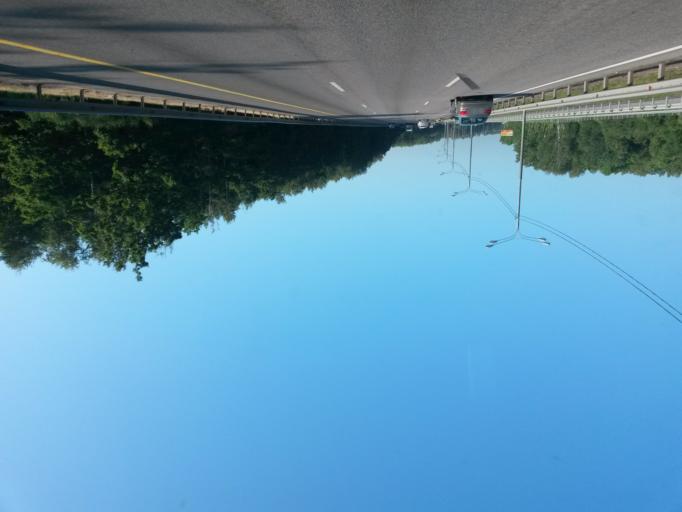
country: RU
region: Moskovskaya
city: Vostryakovo
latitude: 55.3510
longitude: 37.8056
